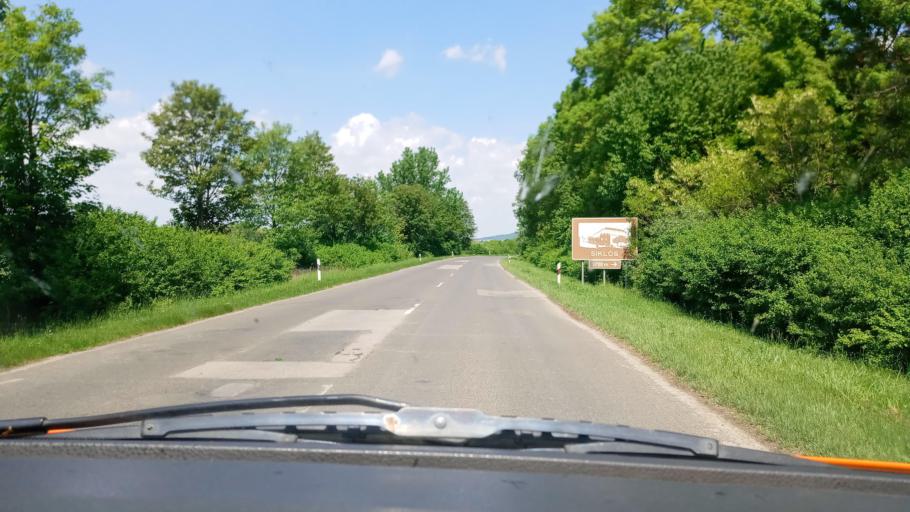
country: HU
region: Baranya
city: Harkany
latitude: 45.8184
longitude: 18.2161
